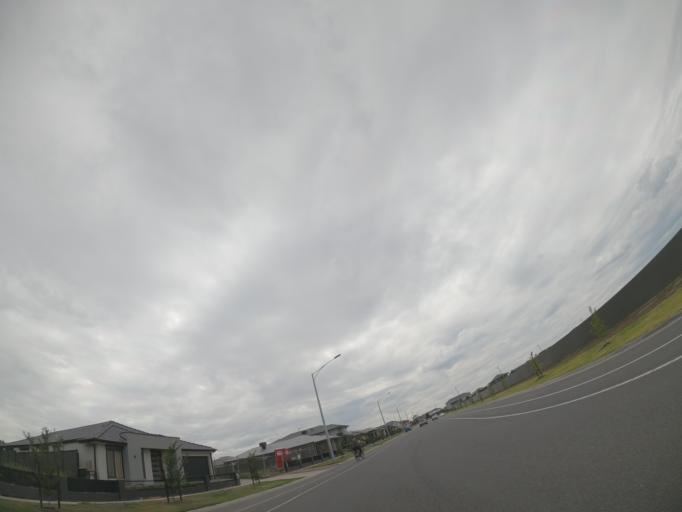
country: AU
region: Victoria
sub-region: Hume
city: Craigieburn
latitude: -37.5718
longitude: 144.8966
